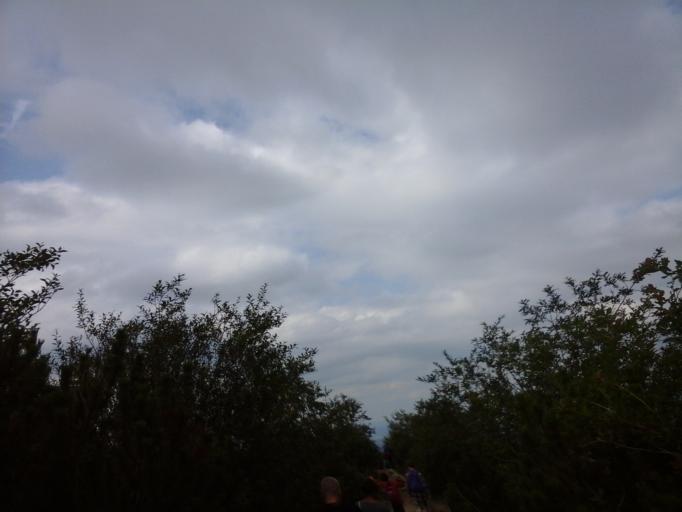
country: PL
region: Lesser Poland Voivodeship
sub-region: Powiat tatrzanski
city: Zakopane
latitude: 49.2500
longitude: 20.0072
